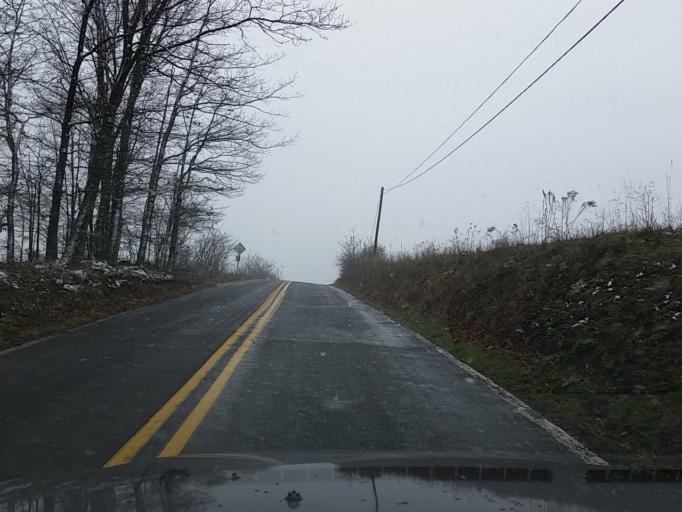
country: US
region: Pennsylvania
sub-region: Luzerne County
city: Glen Lyon
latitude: 41.1994
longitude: -76.1933
